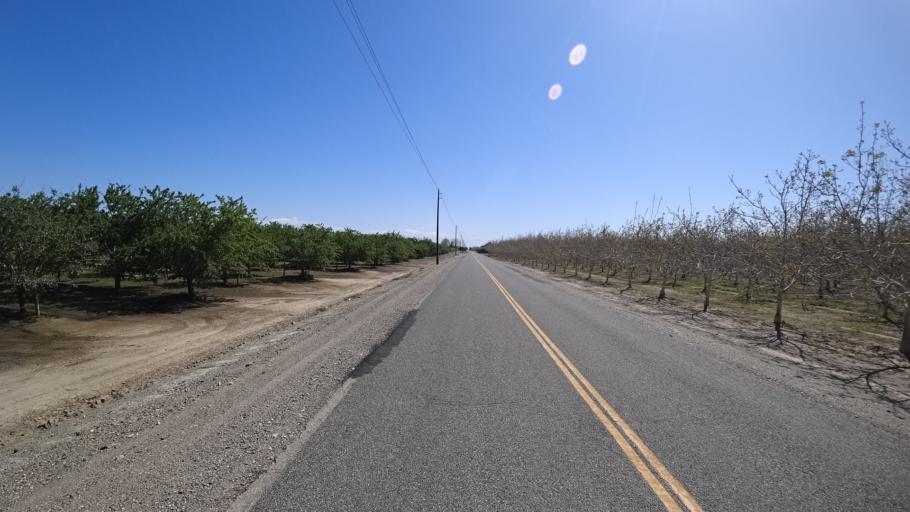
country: US
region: California
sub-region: Glenn County
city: Orland
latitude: 39.7108
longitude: -122.1580
